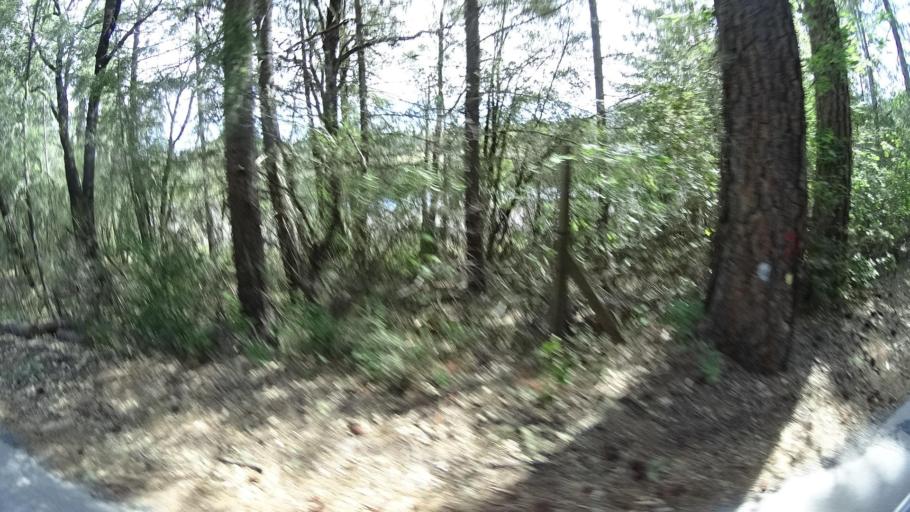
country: US
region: California
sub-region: Lake County
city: Cobb
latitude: 38.8845
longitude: -122.7810
